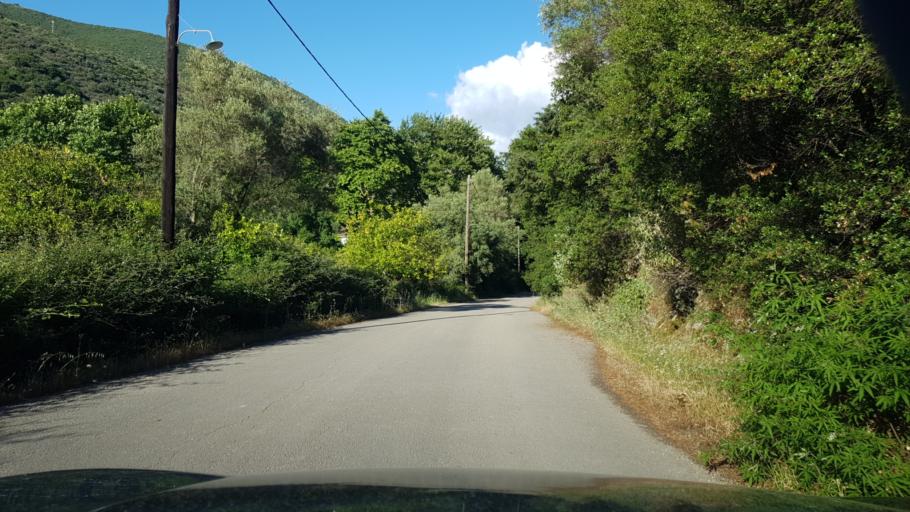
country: GR
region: Ionian Islands
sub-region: Lefkada
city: Nidri
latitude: 38.7154
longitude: 20.6978
